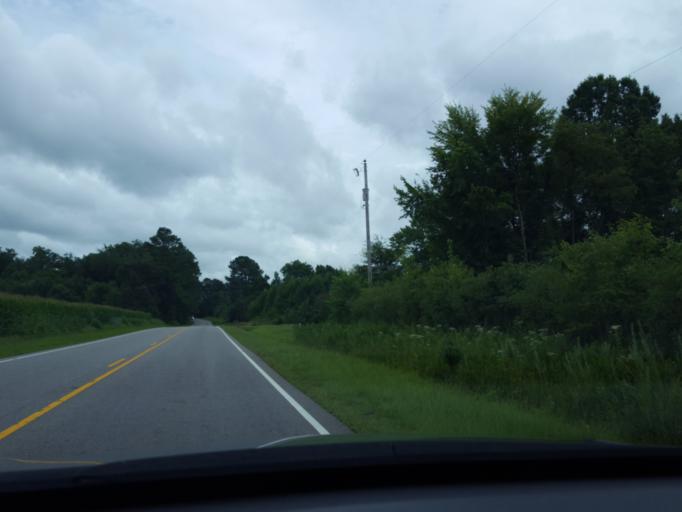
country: US
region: North Carolina
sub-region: Martin County
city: Williamston
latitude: 35.7762
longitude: -76.9283
